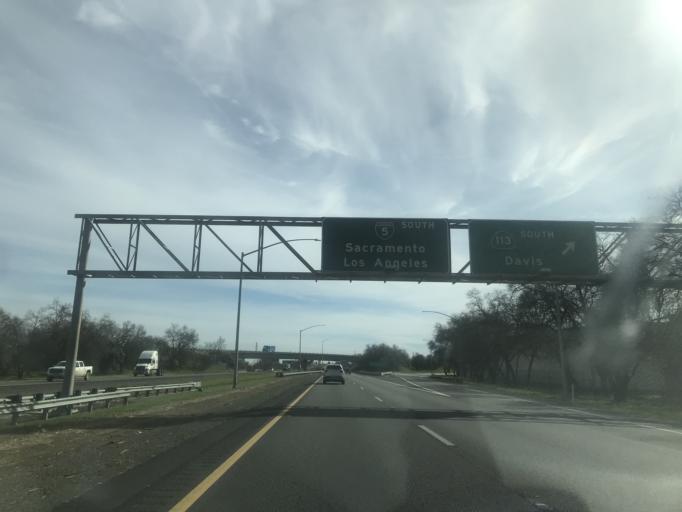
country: US
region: California
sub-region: Yolo County
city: Woodland
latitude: 38.6863
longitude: -121.7525
